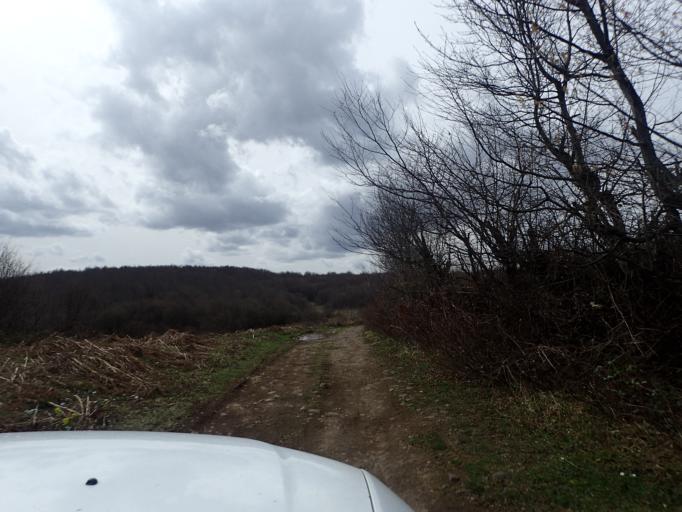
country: TR
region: Ordu
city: Kumru
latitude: 40.8205
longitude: 37.1690
